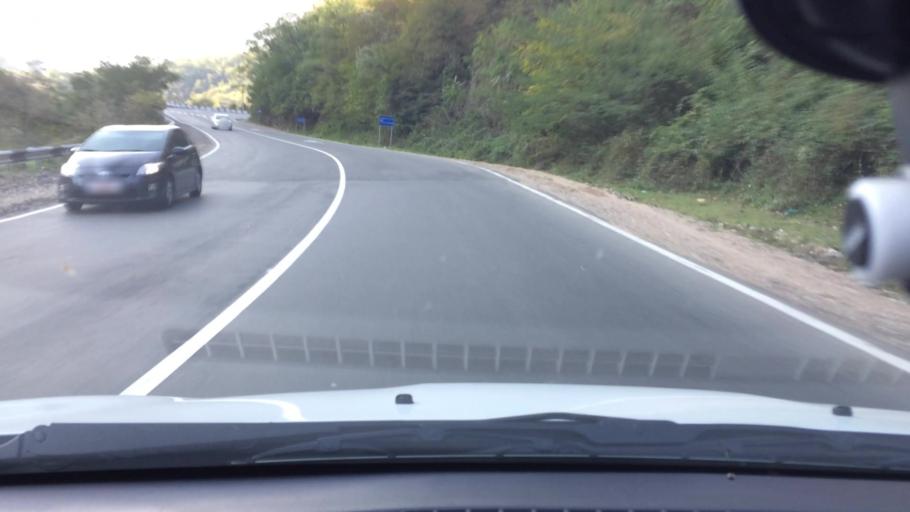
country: GE
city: Shorapani
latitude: 42.0866
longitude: 43.1562
